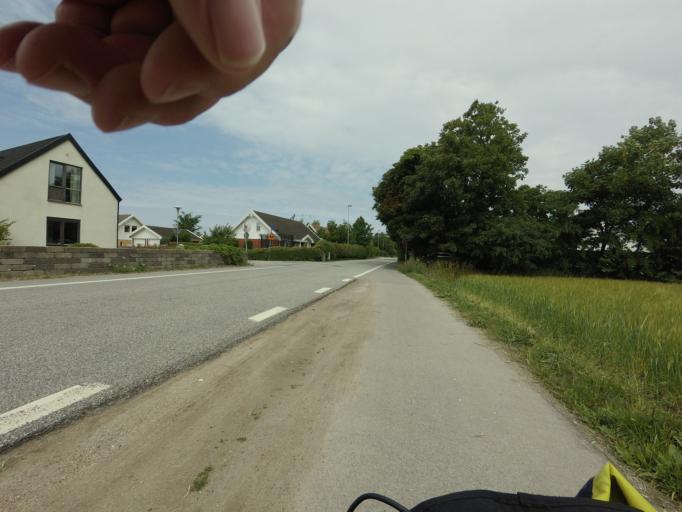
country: SE
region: Skane
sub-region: Malmo
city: Bunkeflostrand
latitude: 55.5337
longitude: 12.9226
